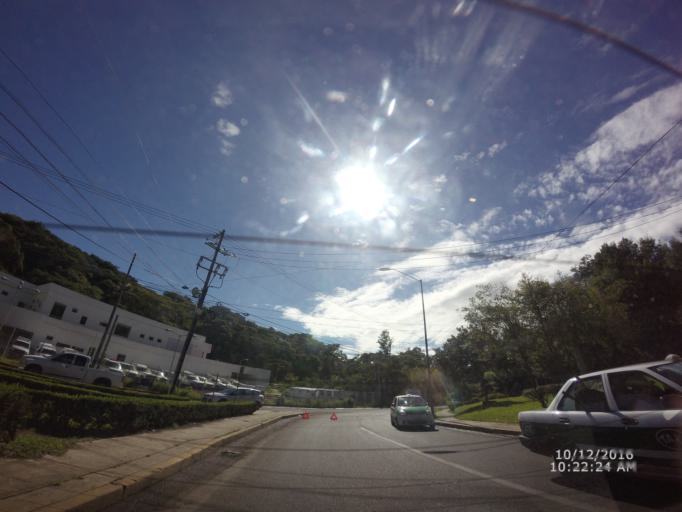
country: TR
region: Sivas
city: Karayun
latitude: 39.6708
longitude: 37.2640
